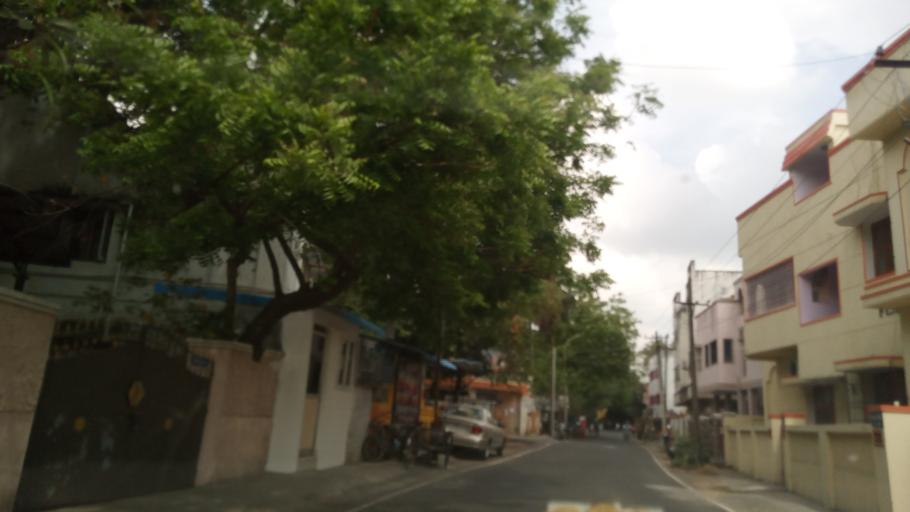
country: IN
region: Tamil Nadu
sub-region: Kancheepuram
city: Madipakkam
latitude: 12.9803
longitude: 80.1816
